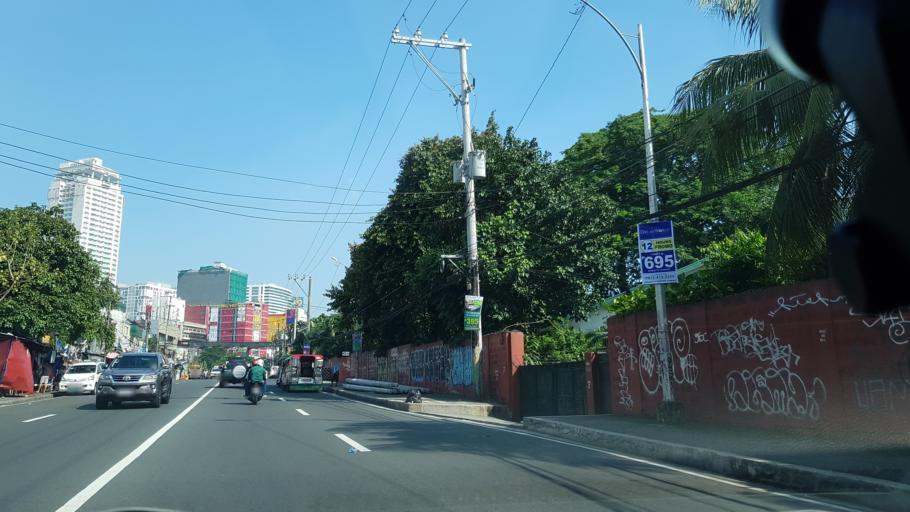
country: PH
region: Metro Manila
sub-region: San Juan
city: San Juan
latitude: 14.6224
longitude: 121.0465
